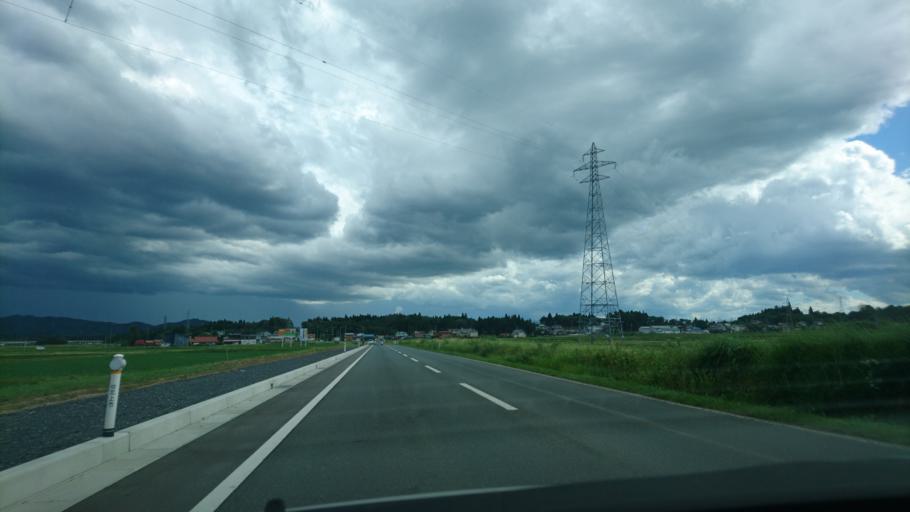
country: JP
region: Iwate
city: Kitakami
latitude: 39.3172
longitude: 141.1269
